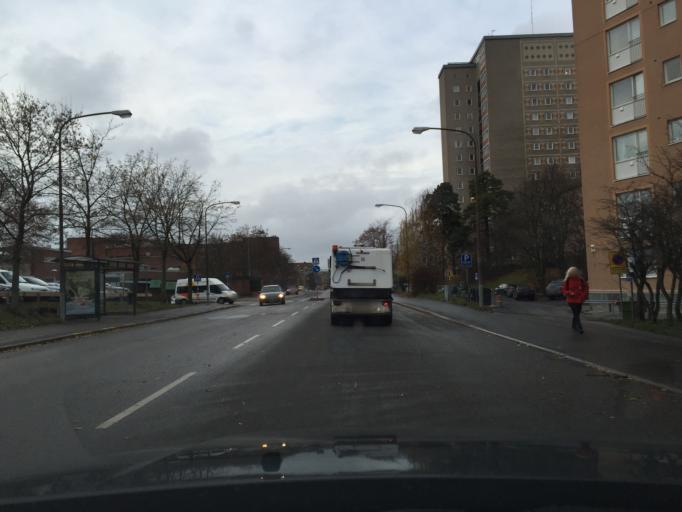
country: SE
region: Stockholm
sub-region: Solna Kommun
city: Solna
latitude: 59.3349
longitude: 18.0218
